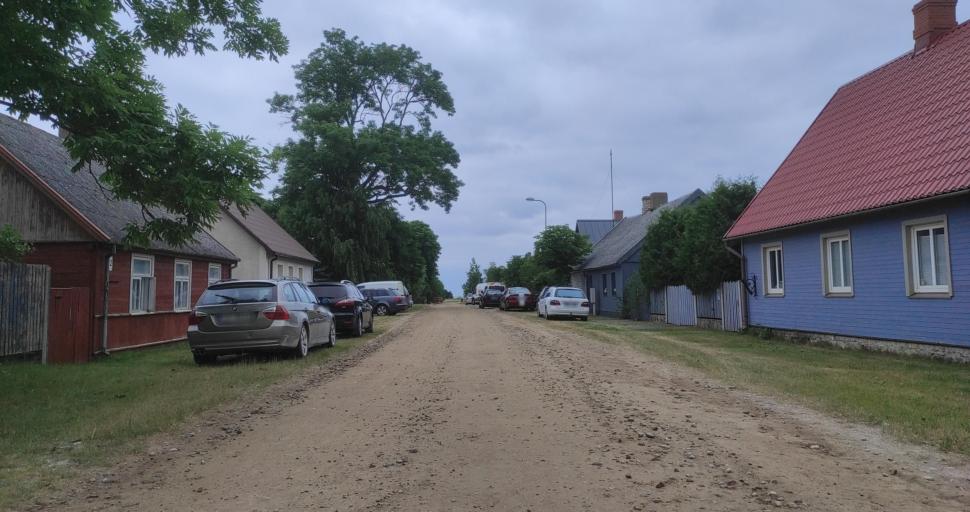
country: LV
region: Pavilostas
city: Pavilosta
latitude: 56.8901
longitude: 21.1819
